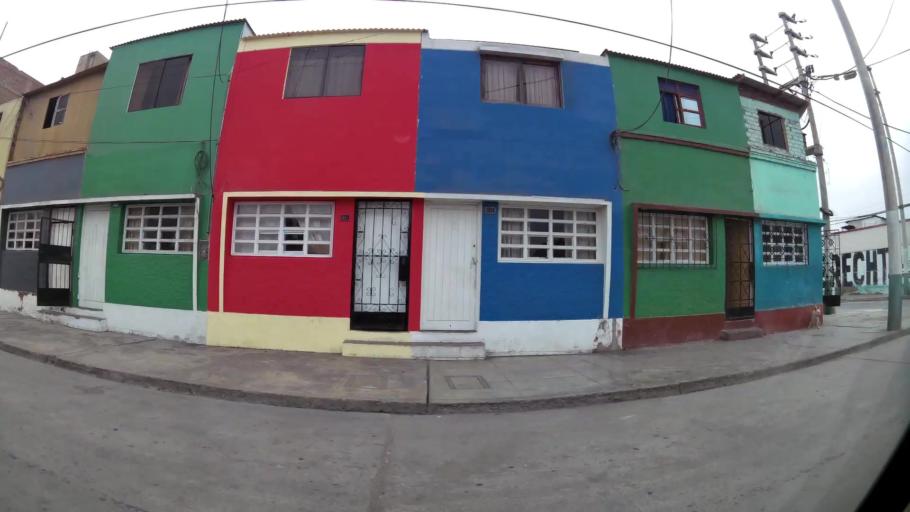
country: PE
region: Callao
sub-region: Callao
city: Callao
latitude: -12.0645
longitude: -77.1439
